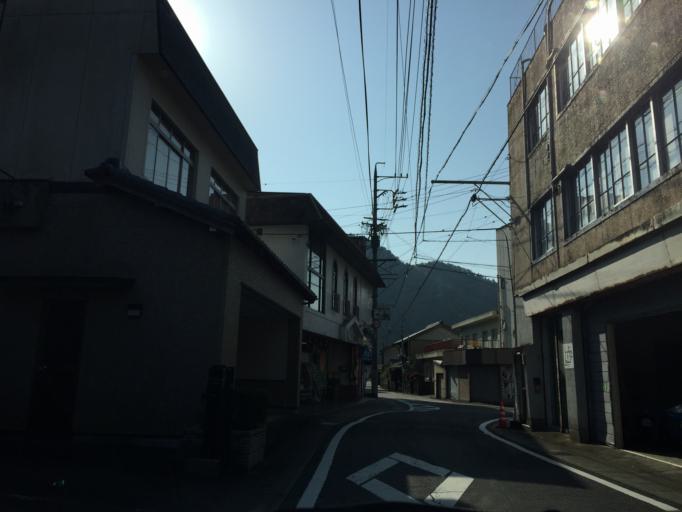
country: JP
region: Gifu
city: Minokamo
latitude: 35.5439
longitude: 137.1208
